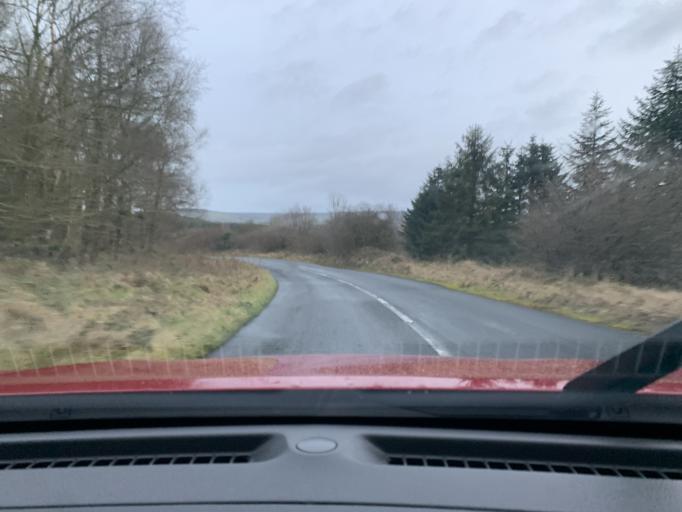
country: IE
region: Connaught
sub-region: Roscommon
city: Boyle
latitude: 54.0128
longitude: -8.3199
